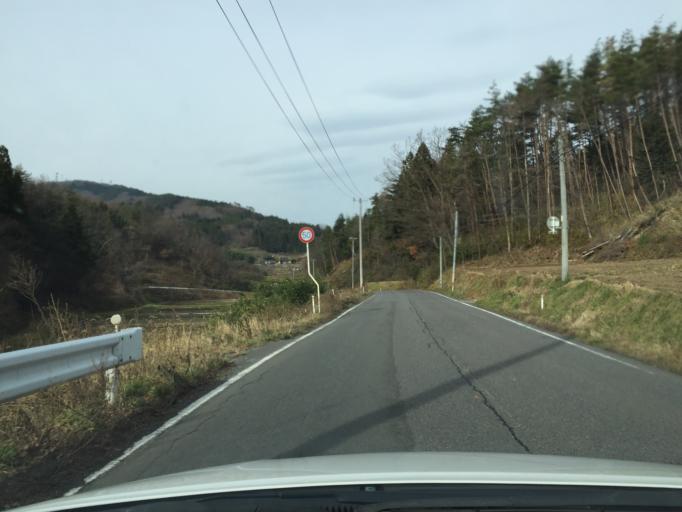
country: JP
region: Fukushima
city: Funehikimachi-funehiki
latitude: 37.4148
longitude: 140.5853
